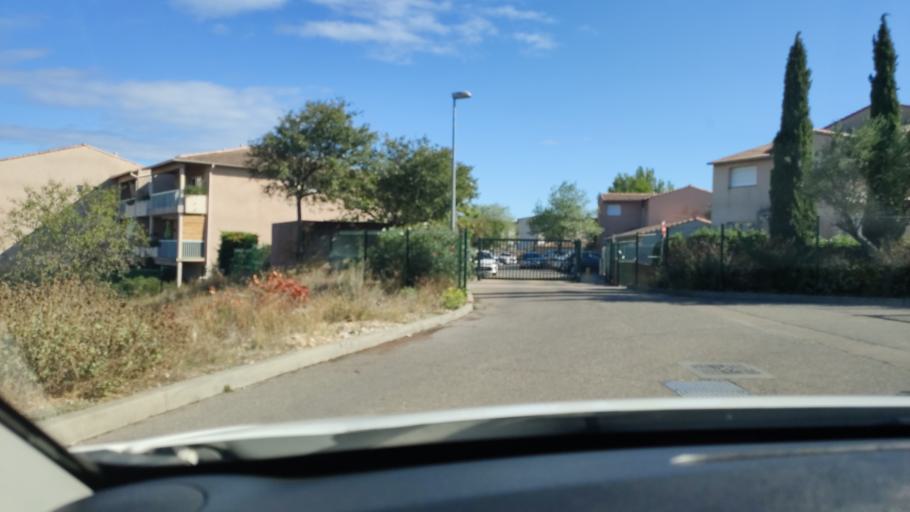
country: FR
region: Languedoc-Roussillon
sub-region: Departement du Gard
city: Villeneuve-les-Avignon
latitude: 43.9797
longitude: 4.7885
